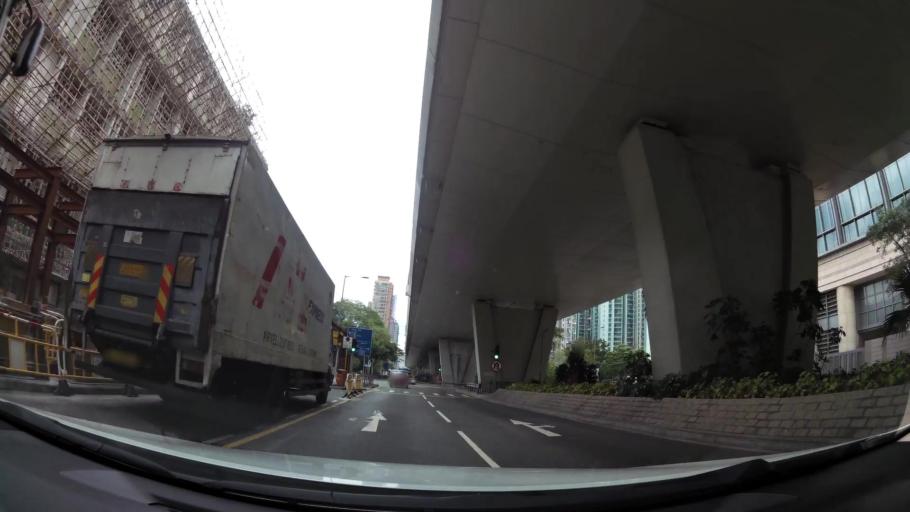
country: HK
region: Sham Shui Po
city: Sham Shui Po
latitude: 22.3314
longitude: 114.1539
